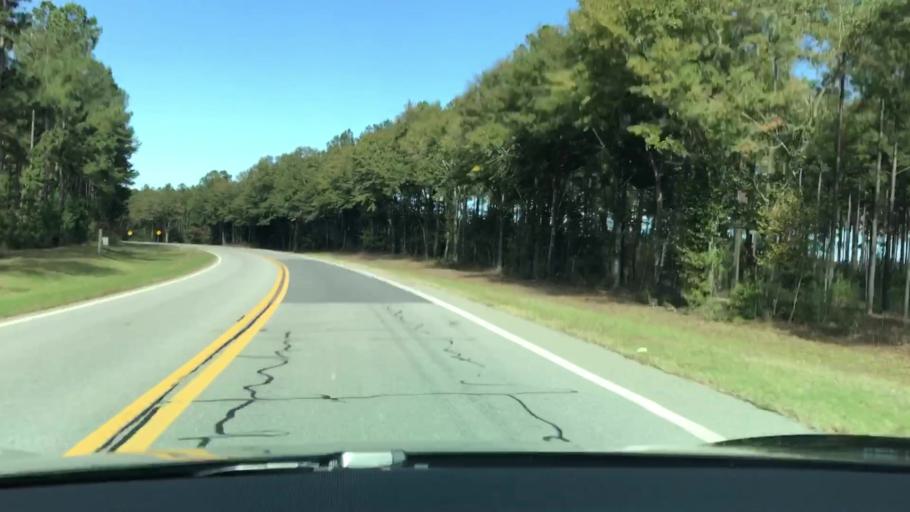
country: US
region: Georgia
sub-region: Warren County
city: Warrenton
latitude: 33.3532
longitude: -82.5873
